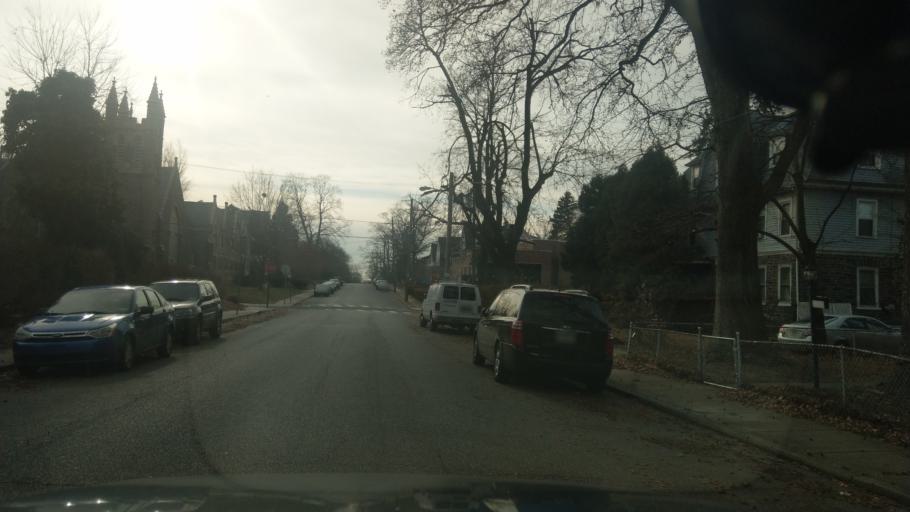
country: US
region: Pennsylvania
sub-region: Montgomery County
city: Wyncote
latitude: 40.0555
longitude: -75.1362
